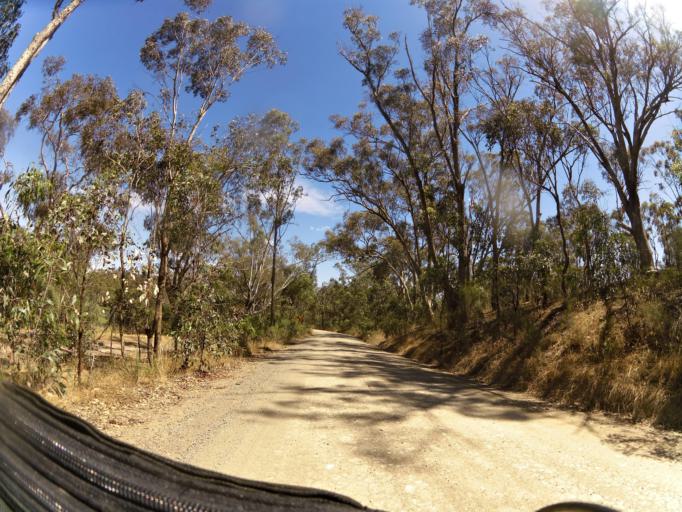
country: AU
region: Victoria
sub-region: Campaspe
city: Kyabram
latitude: -36.8510
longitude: 145.0654
